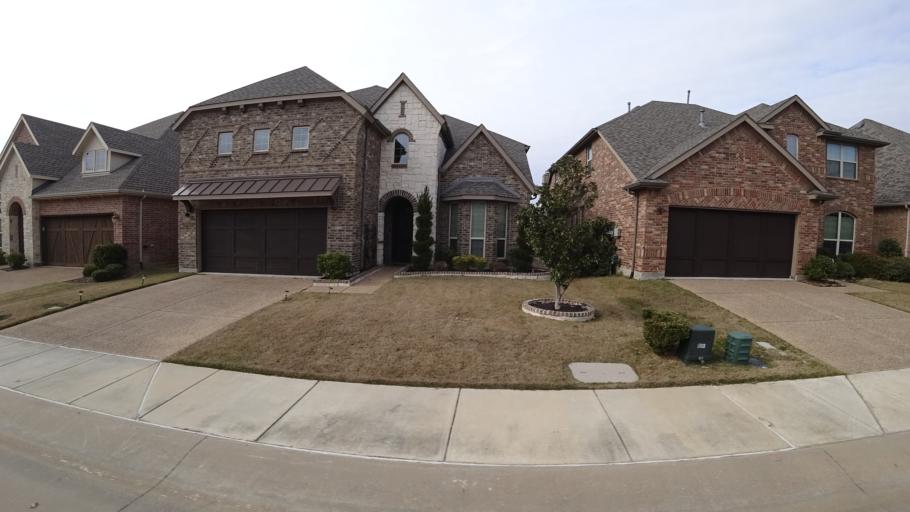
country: US
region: Texas
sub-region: Denton County
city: The Colony
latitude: 33.0552
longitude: -96.9084
